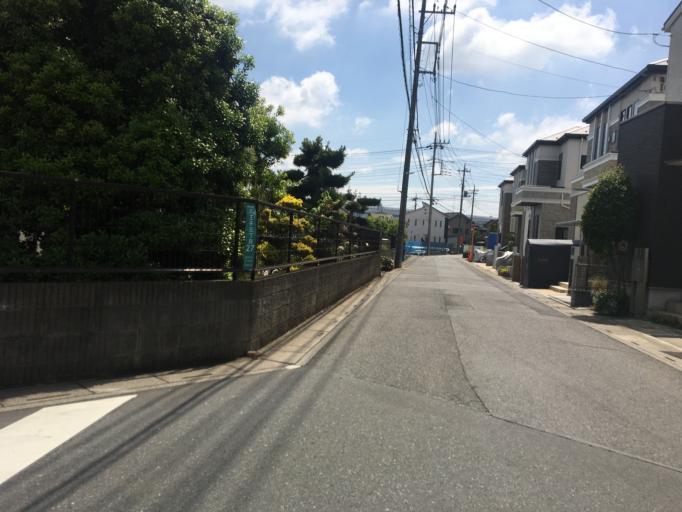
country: JP
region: Saitama
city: Yono
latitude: 35.8819
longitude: 139.6132
